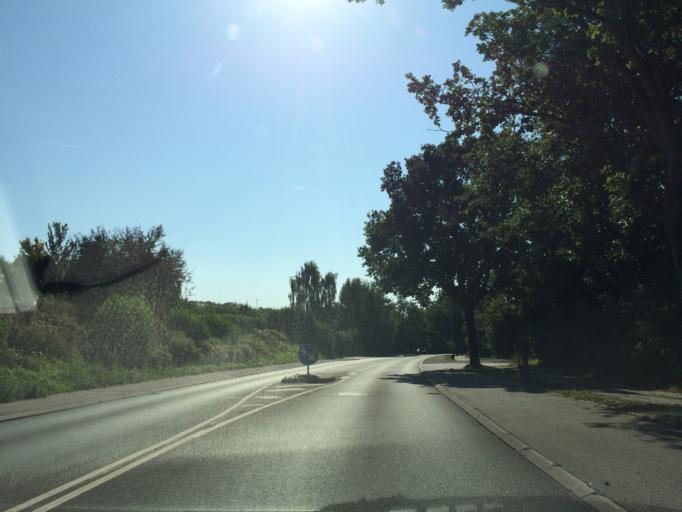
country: DK
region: South Denmark
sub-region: Kolding Kommune
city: Kolding
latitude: 55.5058
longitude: 9.5114
